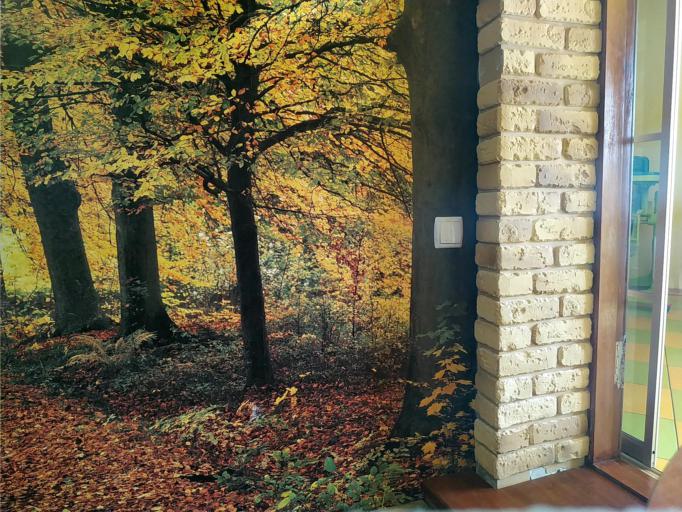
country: RU
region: Smolensk
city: Katyn'
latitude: 54.9982
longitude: 31.7496
